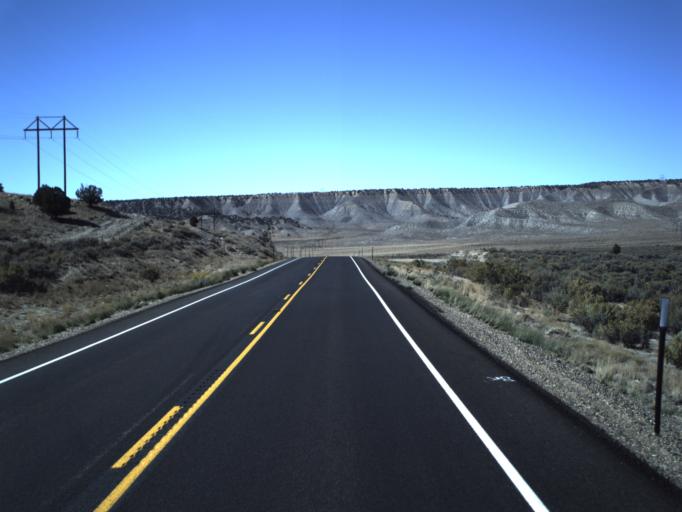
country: US
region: Utah
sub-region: Garfield County
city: Panguitch
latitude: 37.6014
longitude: -111.9586
